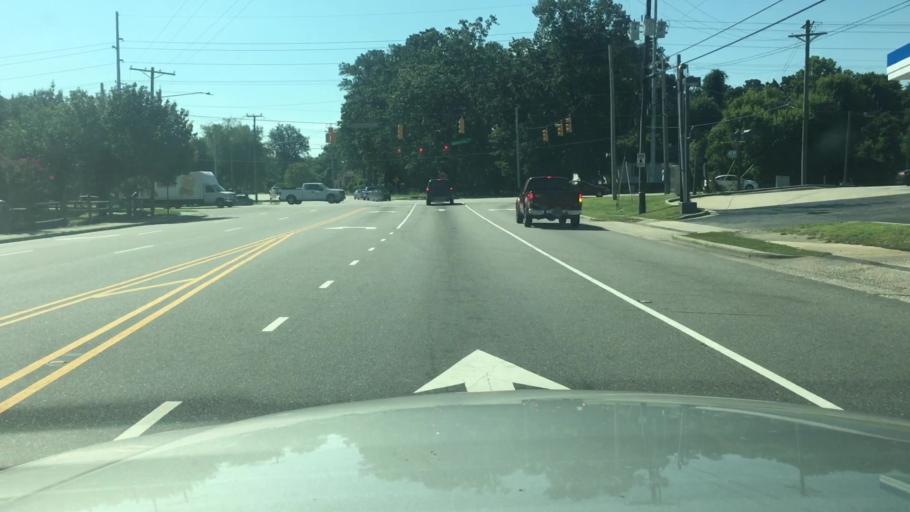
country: US
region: North Carolina
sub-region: Cumberland County
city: Fayetteville
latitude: 35.1033
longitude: -78.8995
